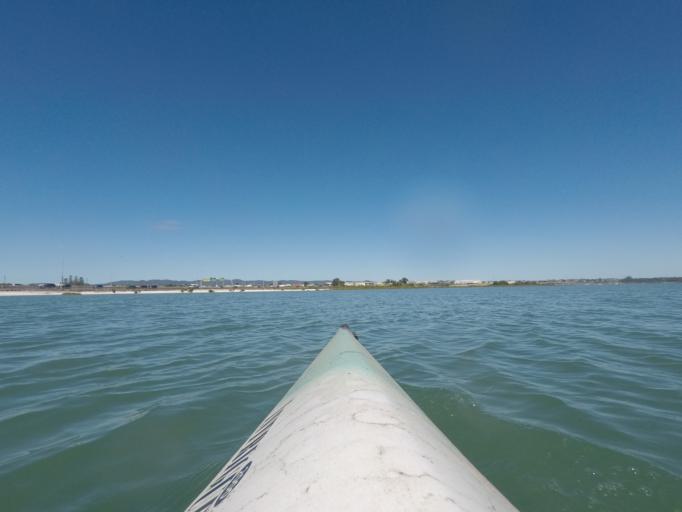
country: NZ
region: Auckland
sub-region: Auckland
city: Rosebank
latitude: -36.8705
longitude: 174.6821
